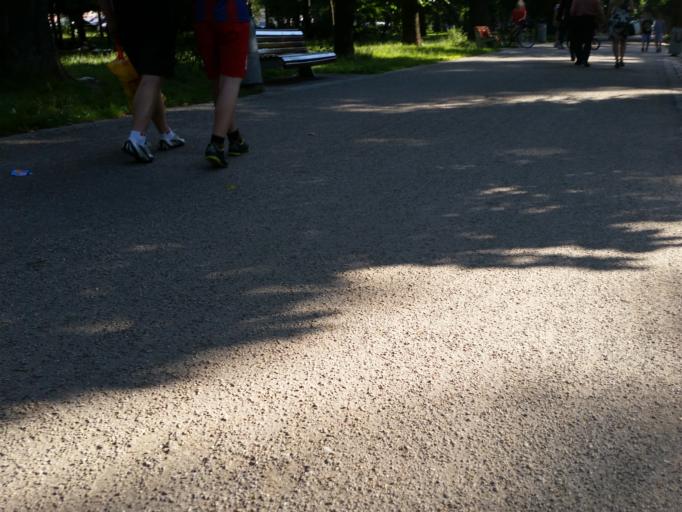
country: RO
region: Cluj
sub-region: Municipiul Cluj-Napoca
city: Cluj-Napoca
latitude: 46.7716
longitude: 23.5825
